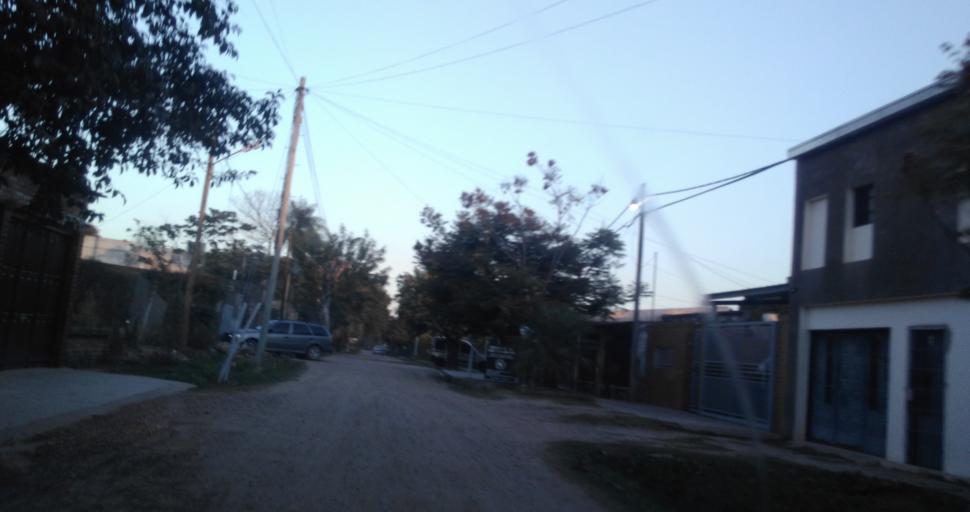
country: AR
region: Chaco
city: Fontana
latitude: -27.4315
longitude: -58.9967
